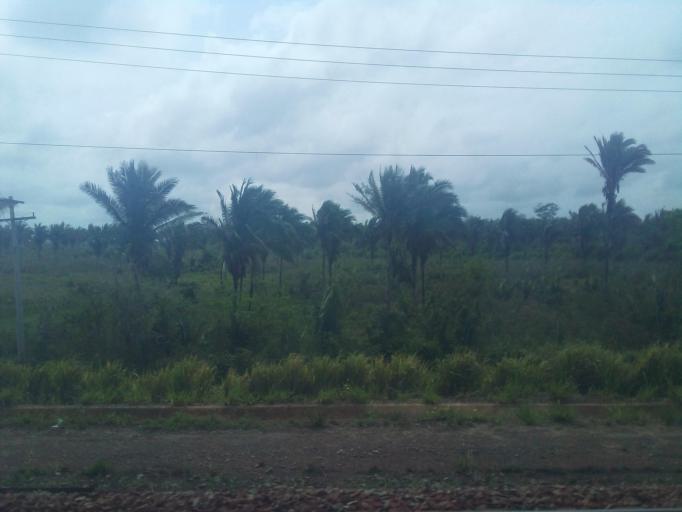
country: BR
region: Maranhao
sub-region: Arari
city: Arari
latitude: -3.4835
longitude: -44.6064
